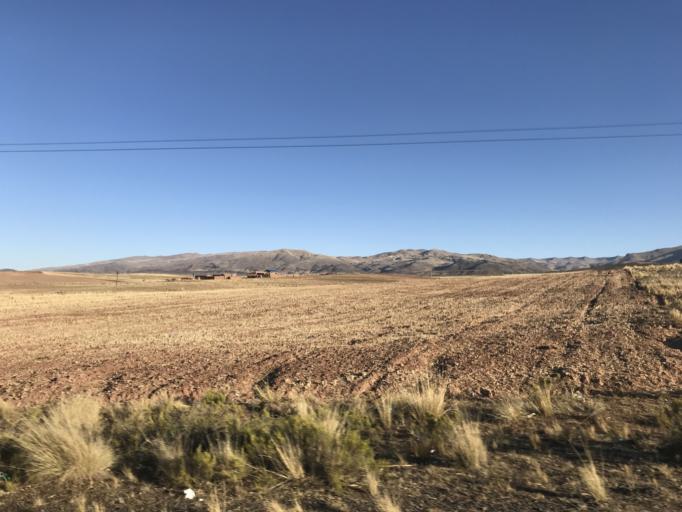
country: BO
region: La Paz
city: Tiahuanaco
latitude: -16.5633
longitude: -68.6287
